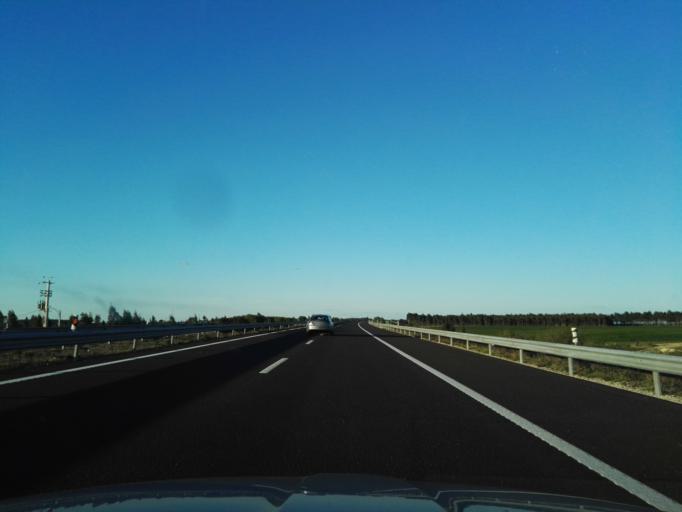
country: PT
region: Santarem
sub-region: Benavente
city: Poceirao
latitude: 38.7548
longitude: -8.6840
